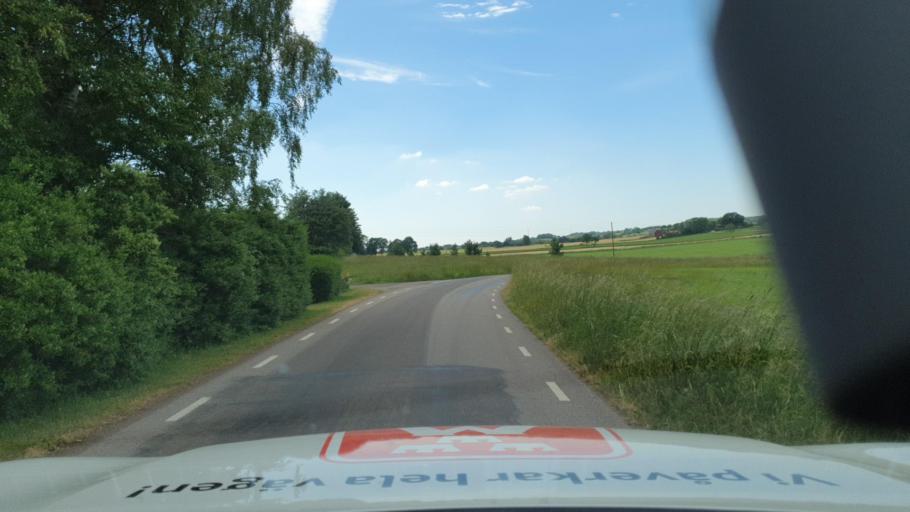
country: SE
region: Skane
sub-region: Sjobo Kommun
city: Sjoebo
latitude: 55.6343
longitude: 13.8104
